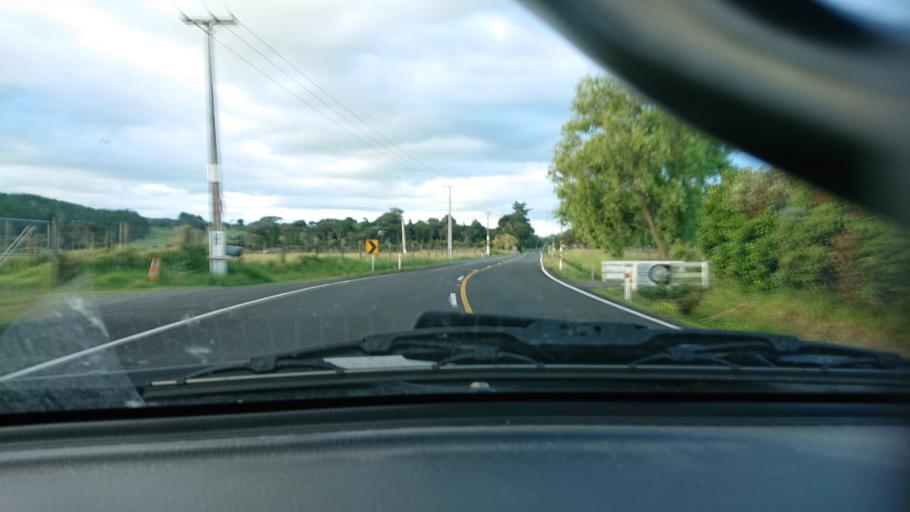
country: NZ
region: Auckland
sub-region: Auckland
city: Parakai
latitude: -36.4957
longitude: 174.4486
